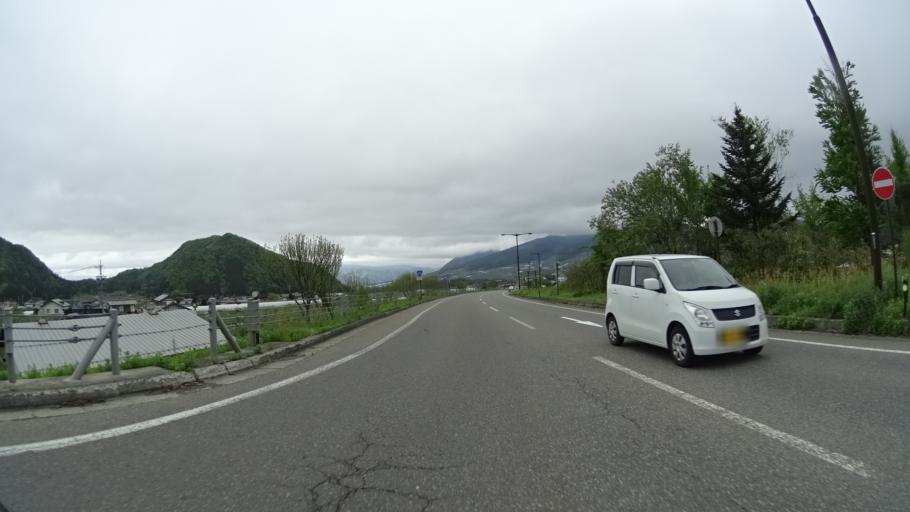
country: JP
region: Nagano
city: Nakano
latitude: 36.7431
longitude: 138.4037
